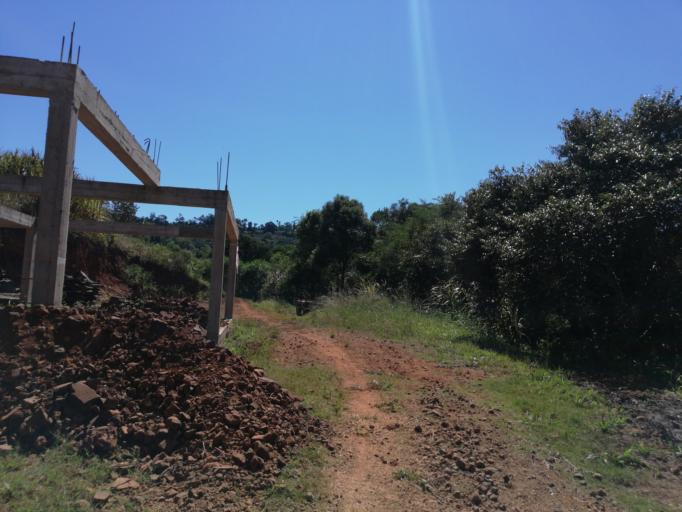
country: AR
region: Misiones
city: Dos de Mayo
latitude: -27.0455
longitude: -54.3999
